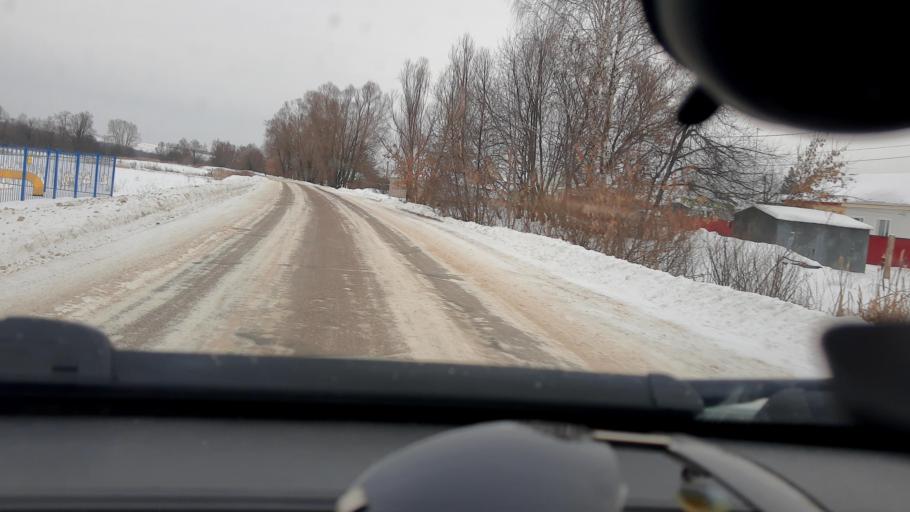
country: RU
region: Bashkortostan
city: Yazykovo
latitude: 55.0401
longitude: 56.1901
